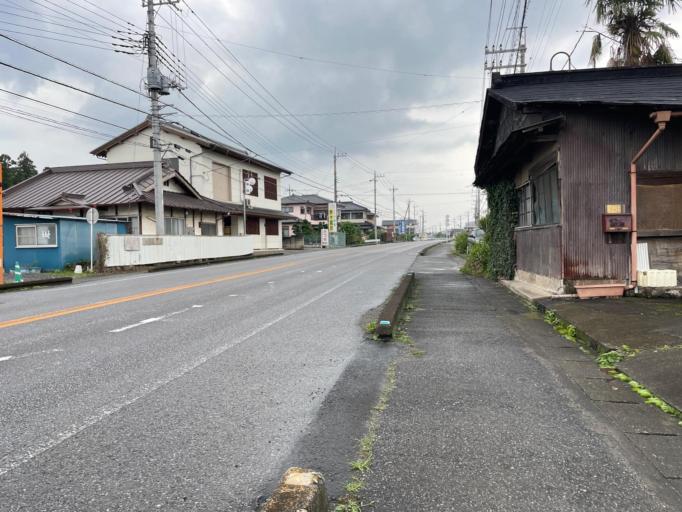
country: JP
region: Tochigi
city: Kanuma
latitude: 36.5220
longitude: 139.7509
